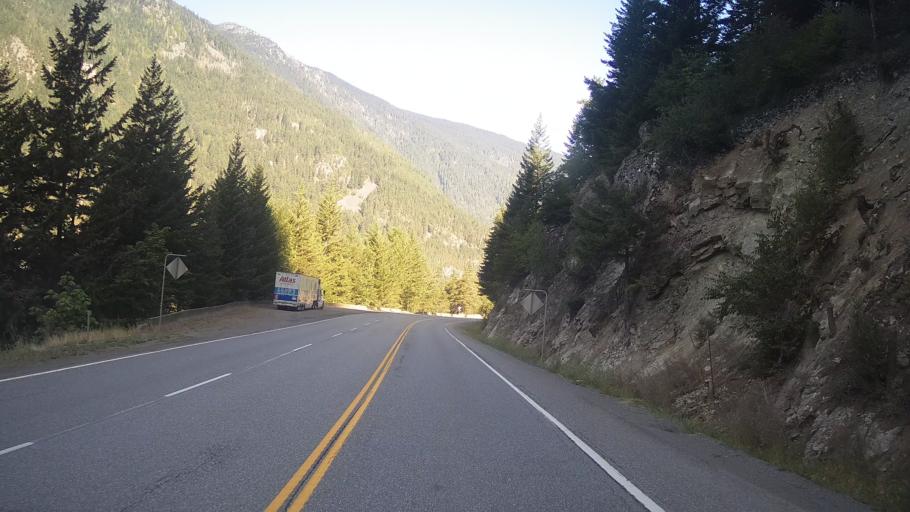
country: CA
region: British Columbia
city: Hope
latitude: 49.7743
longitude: -121.4380
